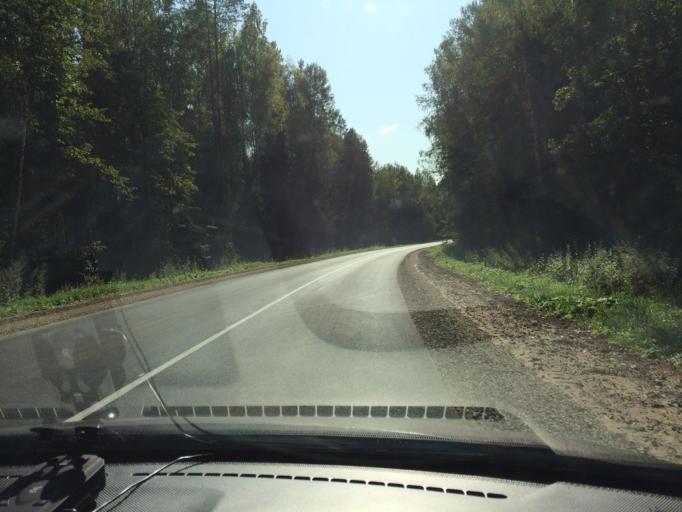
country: RU
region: Mariy-El
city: Surok
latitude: 56.5642
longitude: 48.3015
